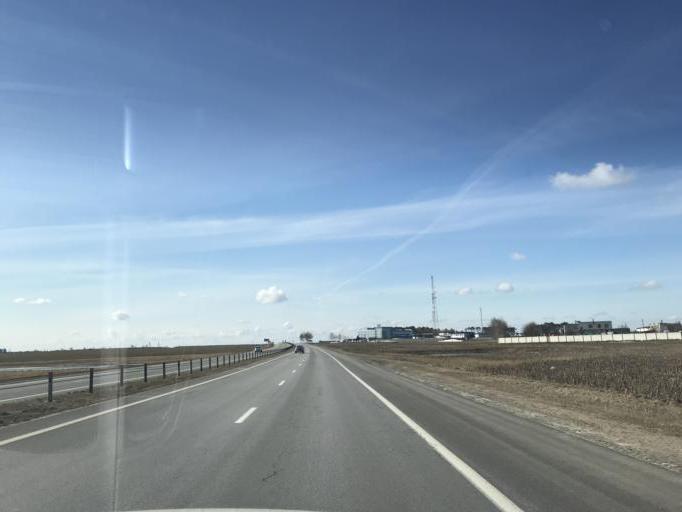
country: BY
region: Gomel
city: Kastsyukowka
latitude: 52.4964
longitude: 30.8627
